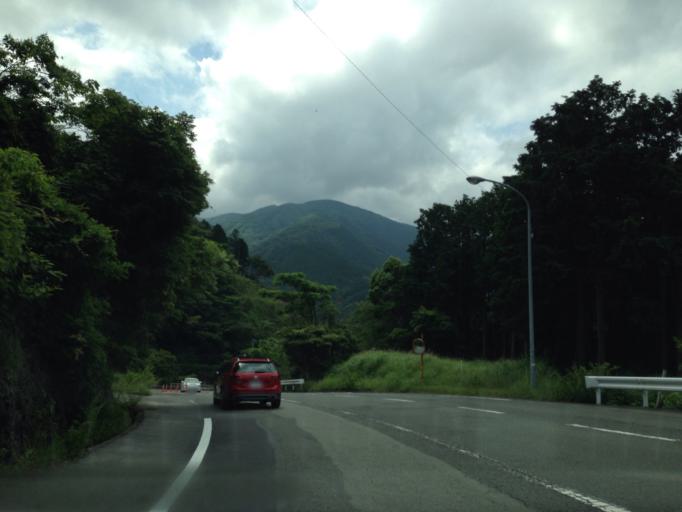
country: JP
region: Shizuoka
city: Heda
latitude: 34.9110
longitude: 138.8171
